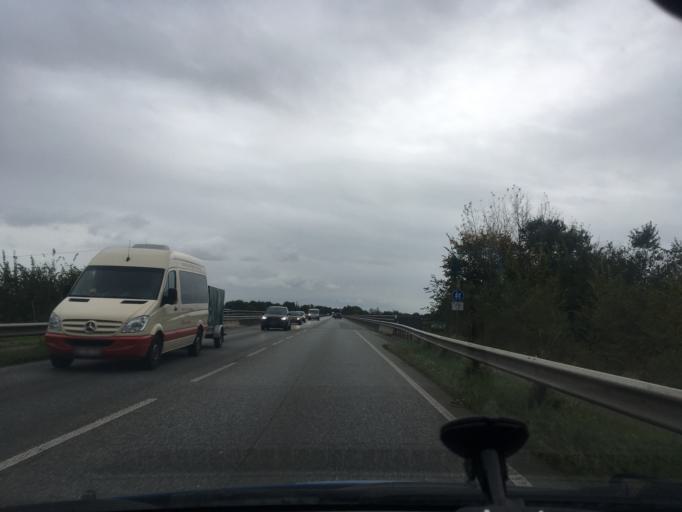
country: DE
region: Lower Saxony
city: Marschacht
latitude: 53.4274
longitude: 10.3354
